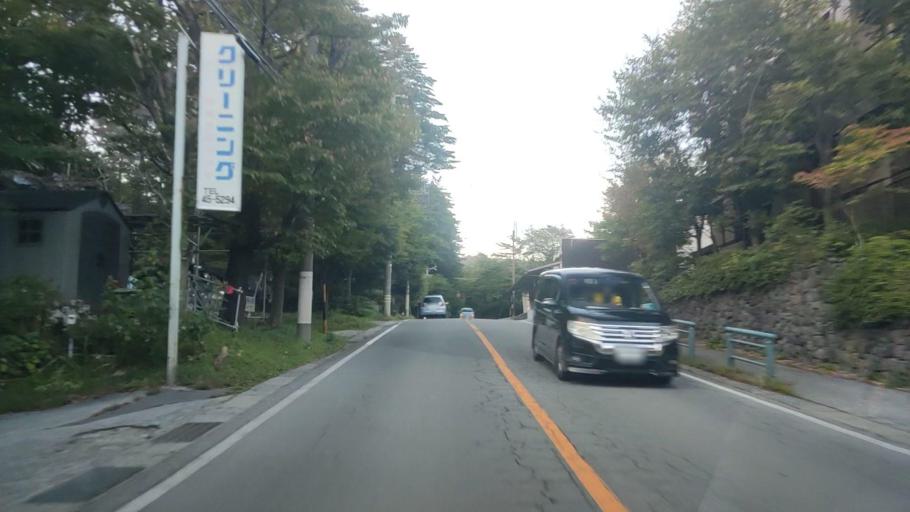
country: JP
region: Nagano
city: Komoro
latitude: 36.3730
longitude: 138.5877
